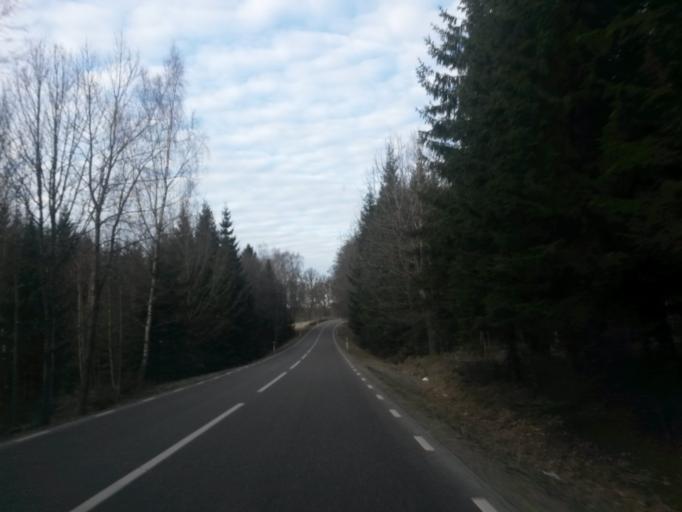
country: SE
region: Vaestra Goetaland
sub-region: Vargarda Kommun
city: Vargarda
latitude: 57.9211
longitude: 12.8695
